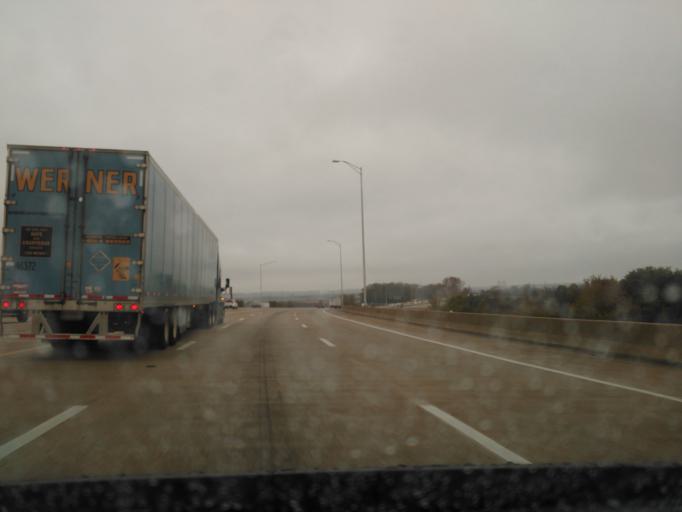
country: US
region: Illinois
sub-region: Monroe County
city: Columbia
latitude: 38.4748
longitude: -90.2321
